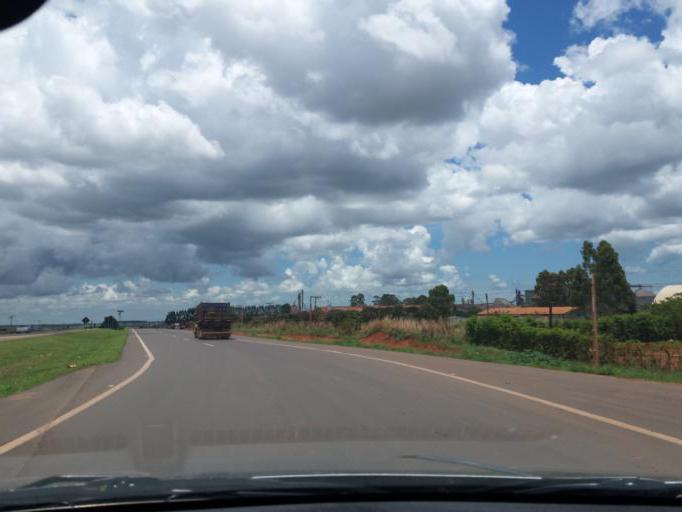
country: BR
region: Goias
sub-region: Cristalina
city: Cristalina
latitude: -16.7793
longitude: -47.6283
